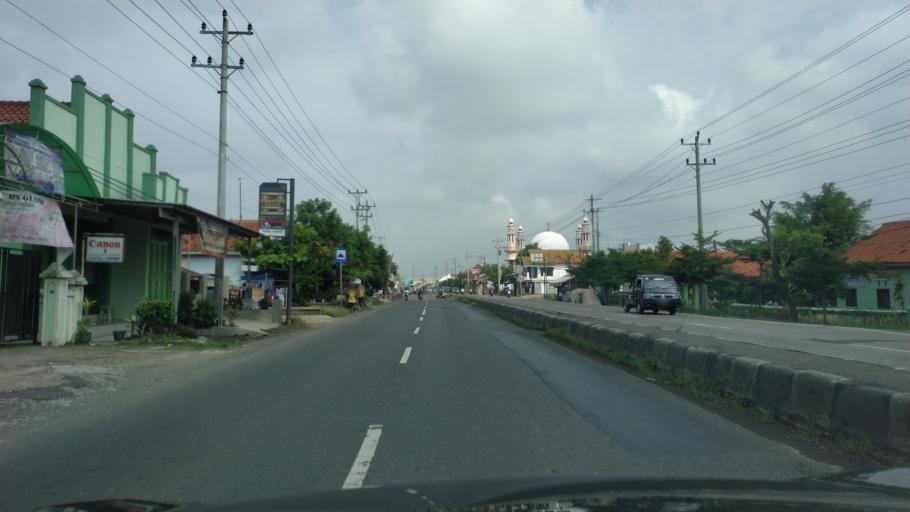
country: ID
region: Central Java
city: Bulakamba
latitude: -6.8746
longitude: 108.9247
